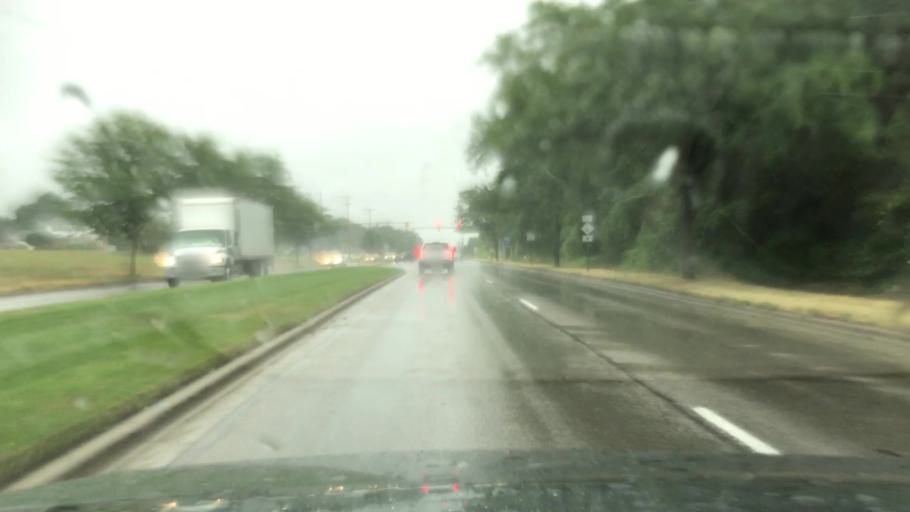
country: US
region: Michigan
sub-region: Kent County
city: Wyoming
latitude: 42.8714
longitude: -85.7235
